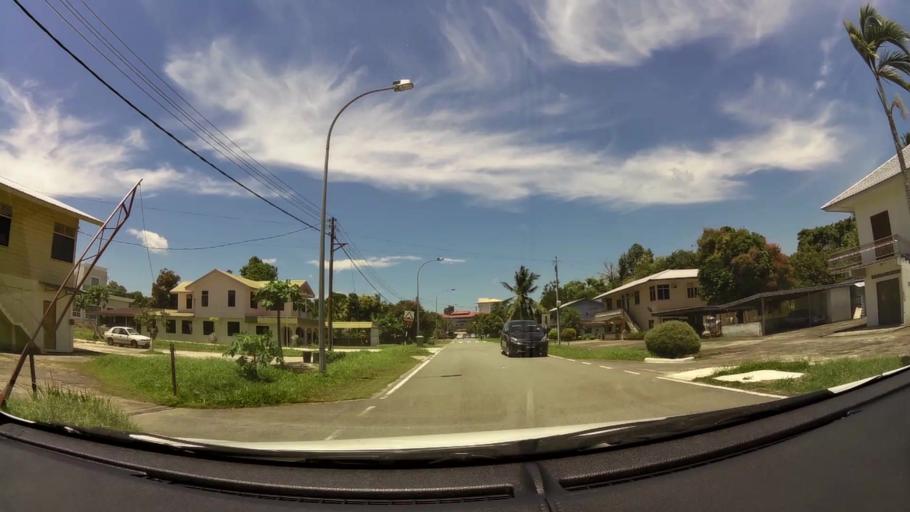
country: BN
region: Brunei and Muara
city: Bandar Seri Begawan
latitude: 4.9300
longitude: 114.9316
